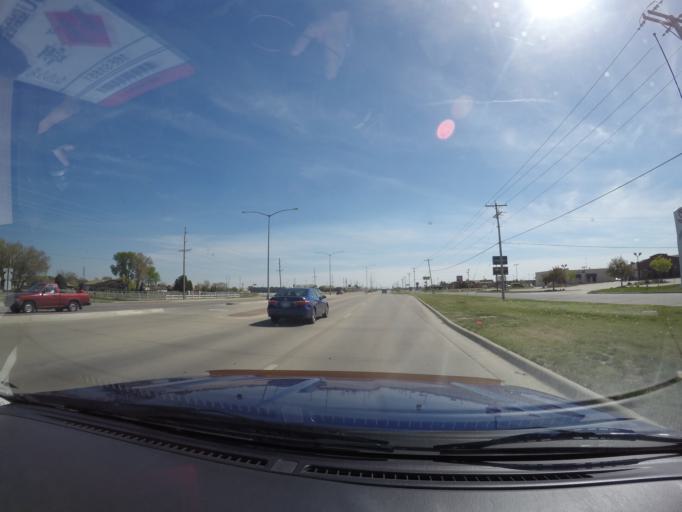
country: US
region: Kansas
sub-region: Saline County
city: Salina
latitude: 38.7897
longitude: -97.6130
